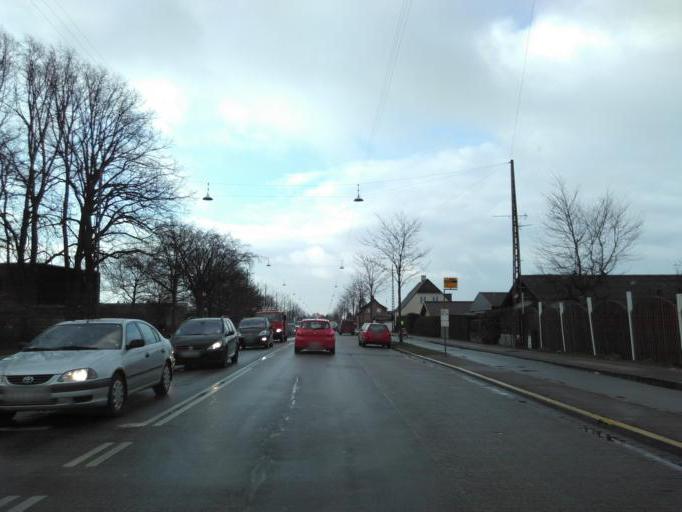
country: DK
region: Capital Region
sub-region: Tarnby Kommune
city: Tarnby
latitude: 55.6460
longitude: 12.5981
